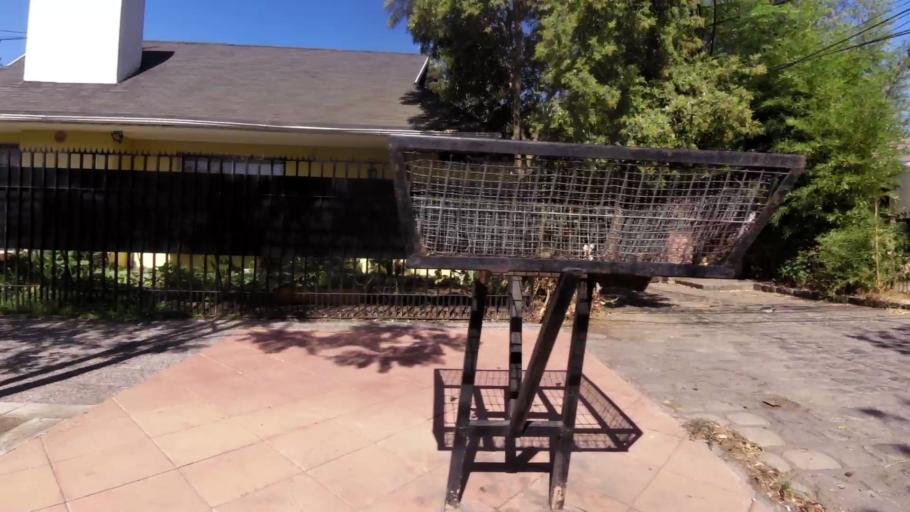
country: CL
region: Maule
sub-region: Provincia de Talca
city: Talca
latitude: -35.4208
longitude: -71.6647
